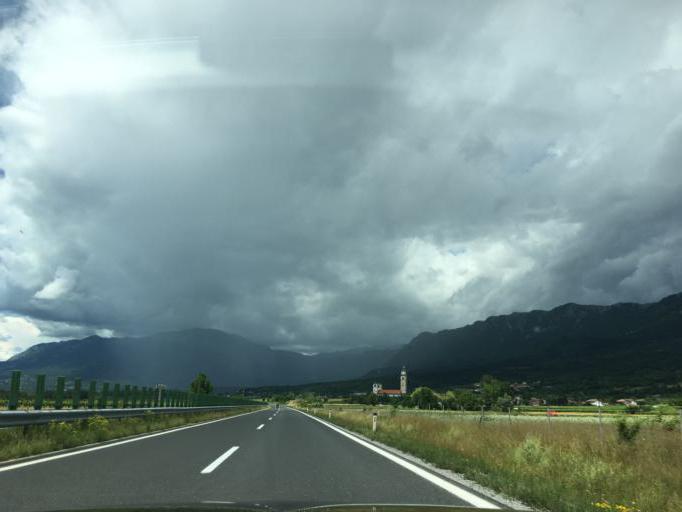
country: SI
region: Vipava
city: Vipava
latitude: 45.8581
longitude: 13.9414
